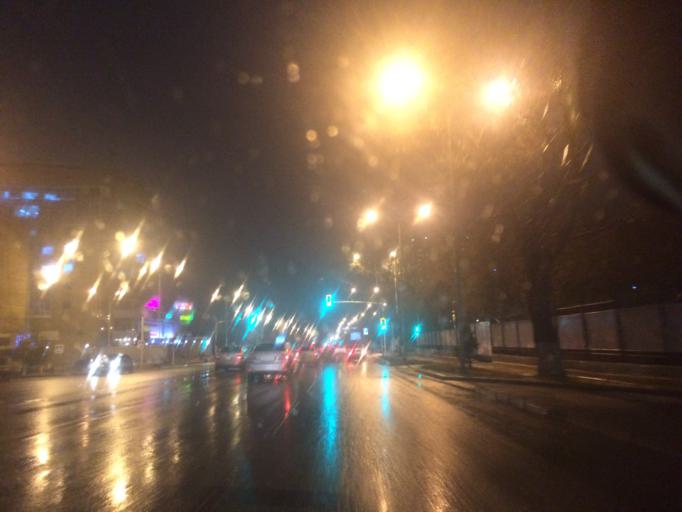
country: KZ
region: Astana Qalasy
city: Astana
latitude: 51.1736
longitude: 71.4252
